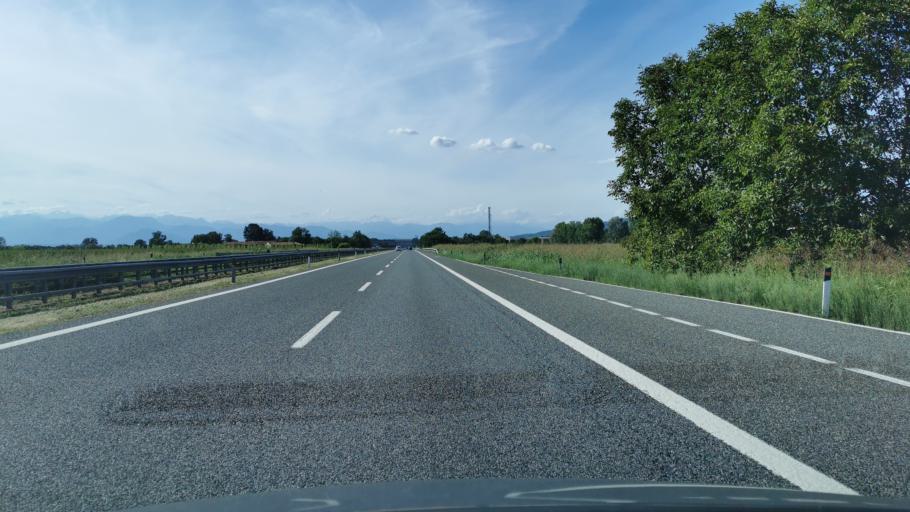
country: IT
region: Piedmont
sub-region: Provincia di Torino
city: Villastellone
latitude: 44.9271
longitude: 7.7286
